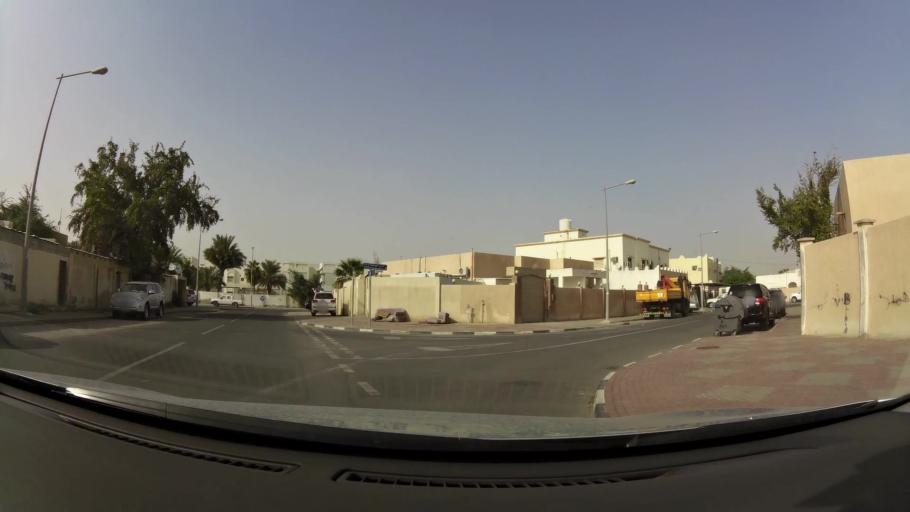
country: QA
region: Baladiyat ar Rayyan
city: Ar Rayyan
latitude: 25.2384
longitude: 51.4389
